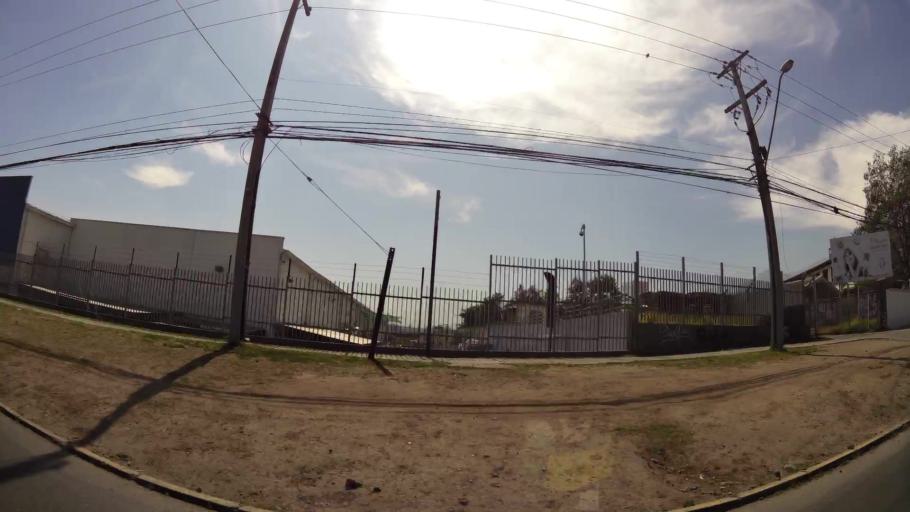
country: CL
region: Santiago Metropolitan
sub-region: Provincia de Santiago
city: Villa Presidente Frei, Nunoa, Santiago, Chile
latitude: -33.4636
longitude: -70.5446
